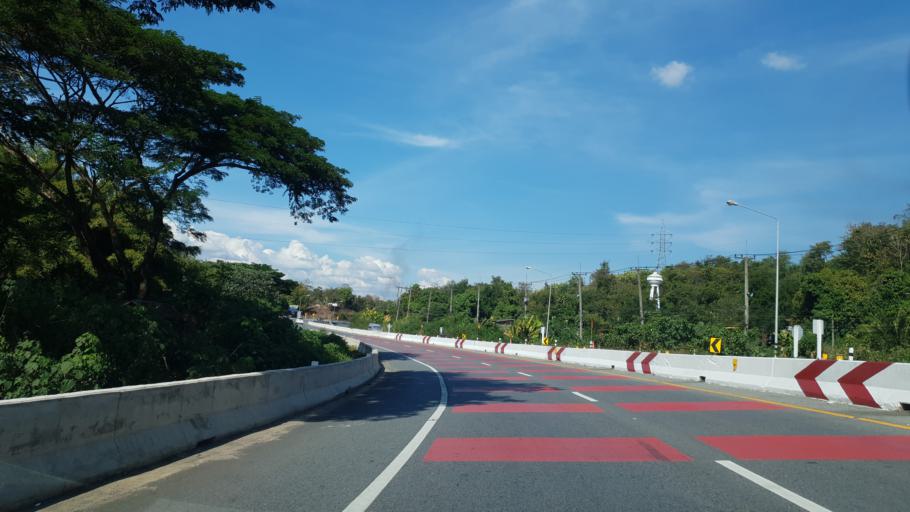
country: TH
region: Phrae
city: Den Chai
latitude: 17.9055
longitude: 100.0657
